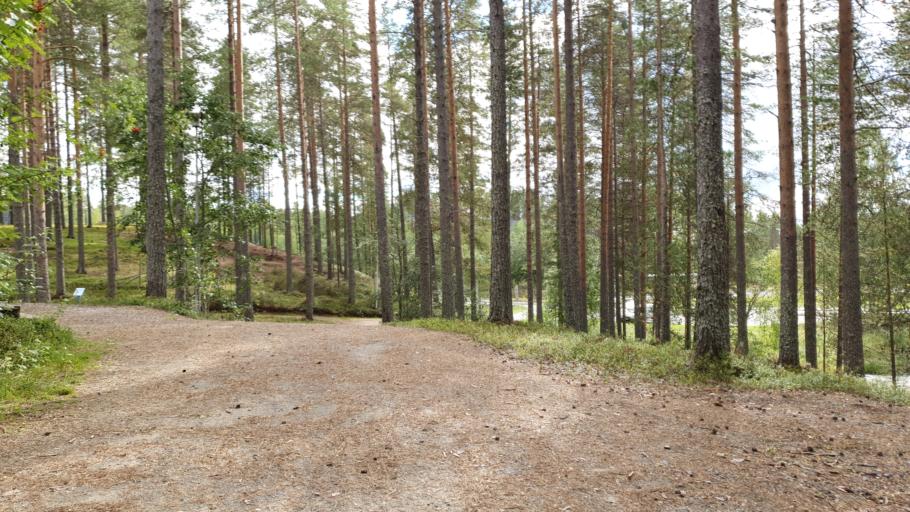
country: FI
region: Kainuu
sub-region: Kehys-Kainuu
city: Kuhmo
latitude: 64.1197
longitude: 29.5861
